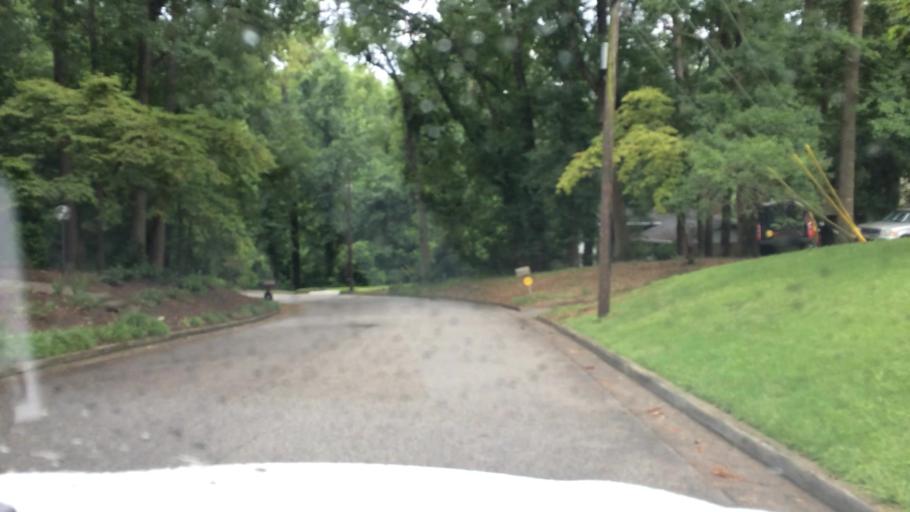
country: US
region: South Carolina
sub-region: Aiken County
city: North Augusta
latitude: 33.5039
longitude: -81.9873
